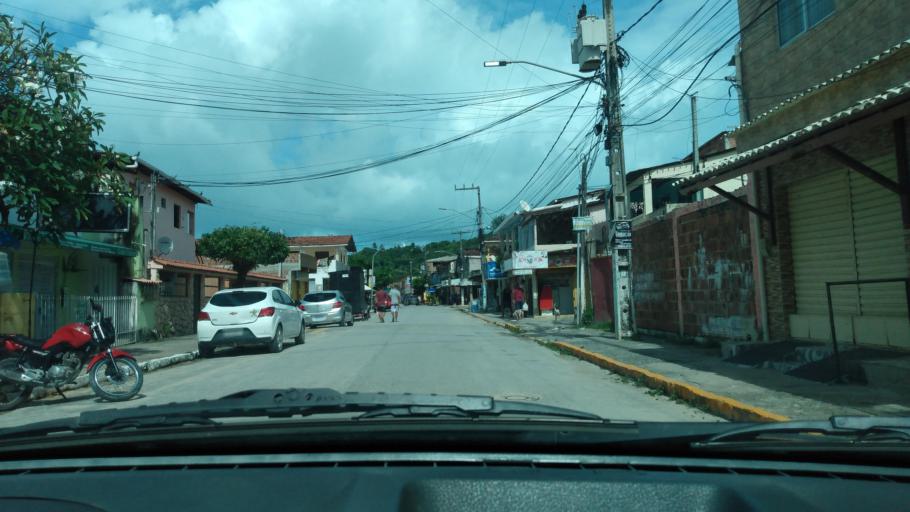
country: BR
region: Pernambuco
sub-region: Cabo De Santo Agostinho
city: Cabo
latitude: -8.3396
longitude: -34.9523
